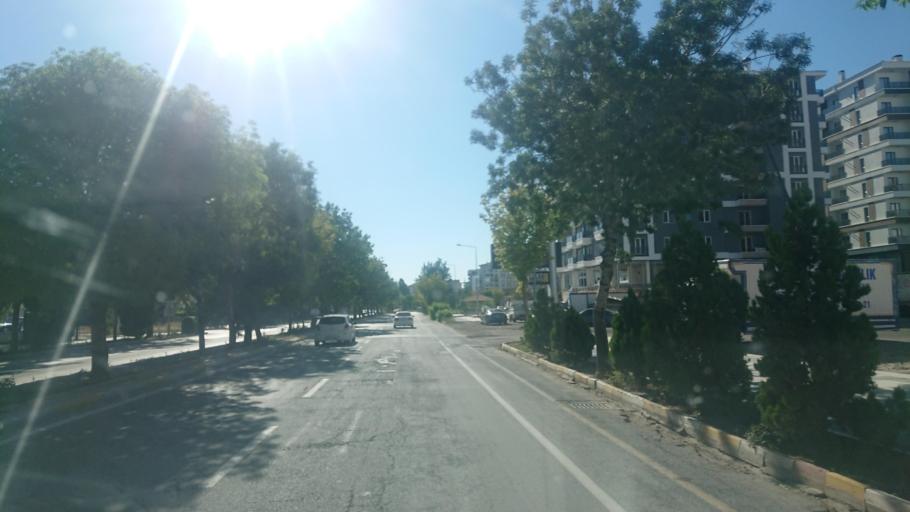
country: TR
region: Aksaray
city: Aksaray
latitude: 38.3643
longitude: 34.0135
